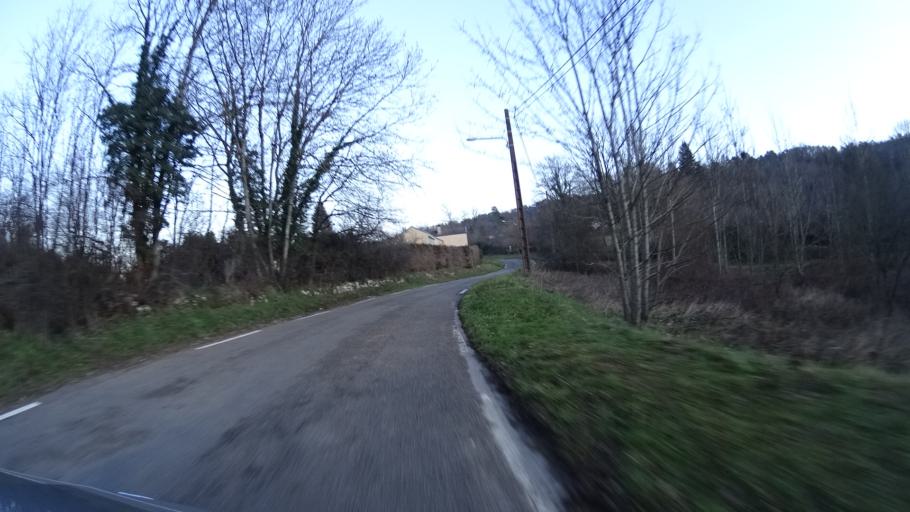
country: FR
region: Franche-Comte
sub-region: Departement du Doubs
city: Besancon
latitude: 47.2234
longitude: 6.0394
